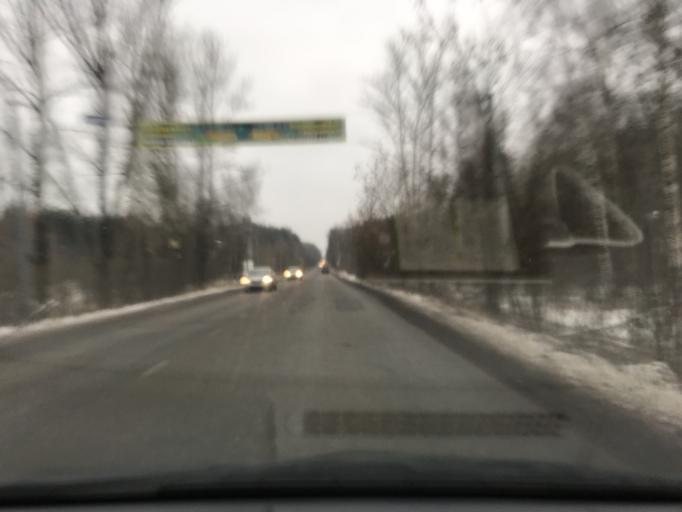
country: RU
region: Moskovskaya
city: Elektrostal'
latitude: 55.8107
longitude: 38.4590
